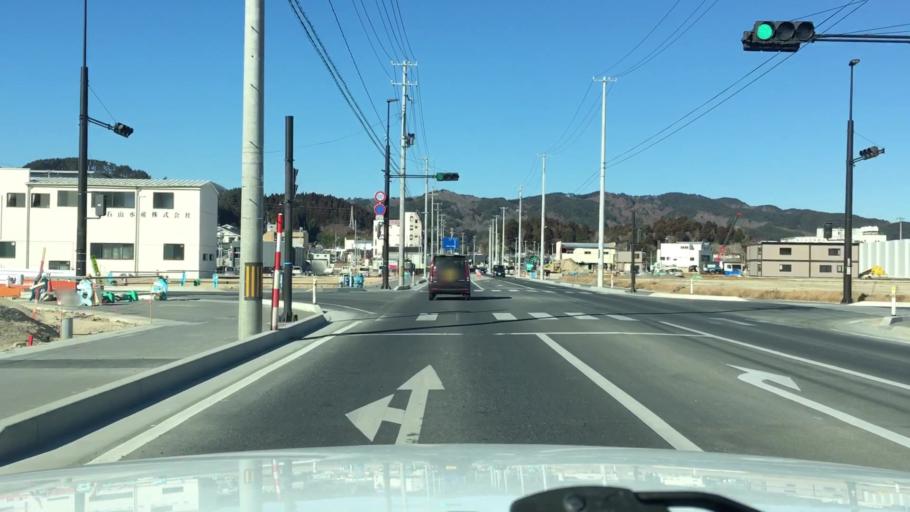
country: JP
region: Iwate
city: Yamada
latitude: 39.4627
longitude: 141.9543
